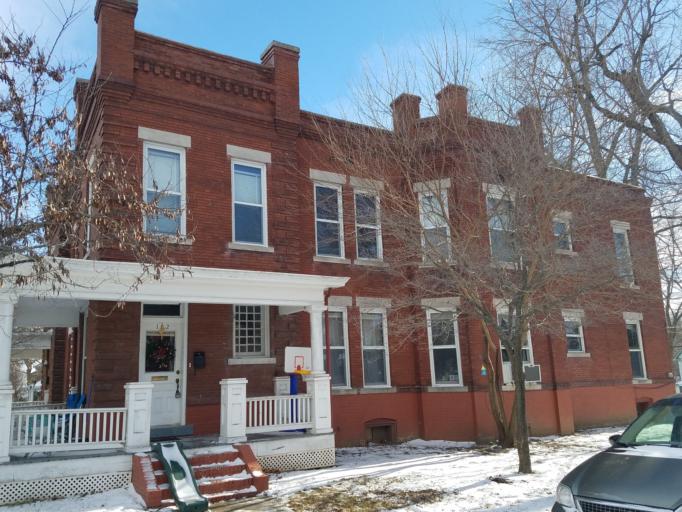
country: US
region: Missouri
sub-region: Lafayette County
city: Lexington
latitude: 39.1852
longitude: -93.8740
